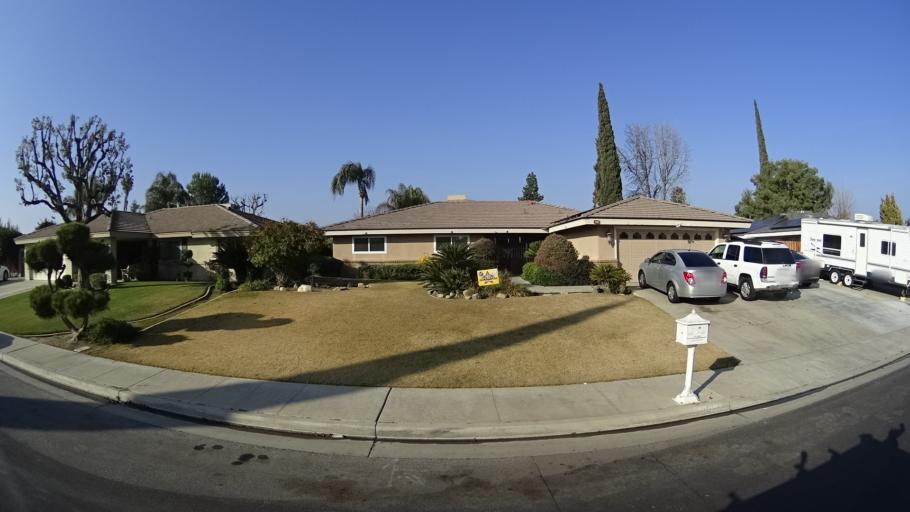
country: US
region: California
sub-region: Kern County
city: Greenacres
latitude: 35.3309
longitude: -119.0703
